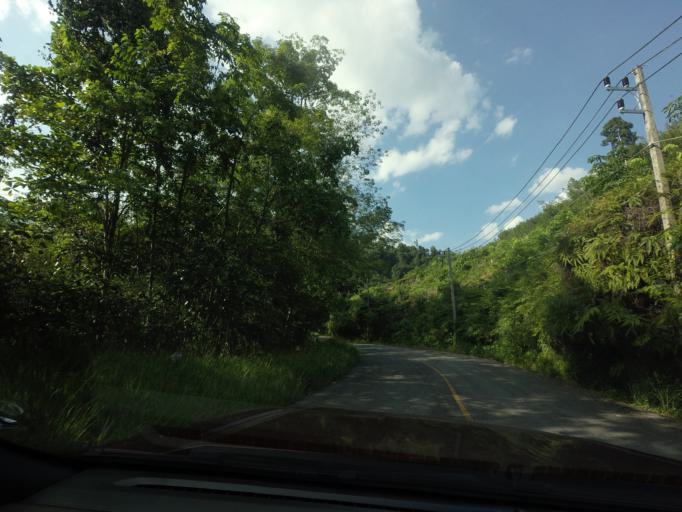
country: TH
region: Yala
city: Than To
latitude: 6.1365
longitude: 101.2915
